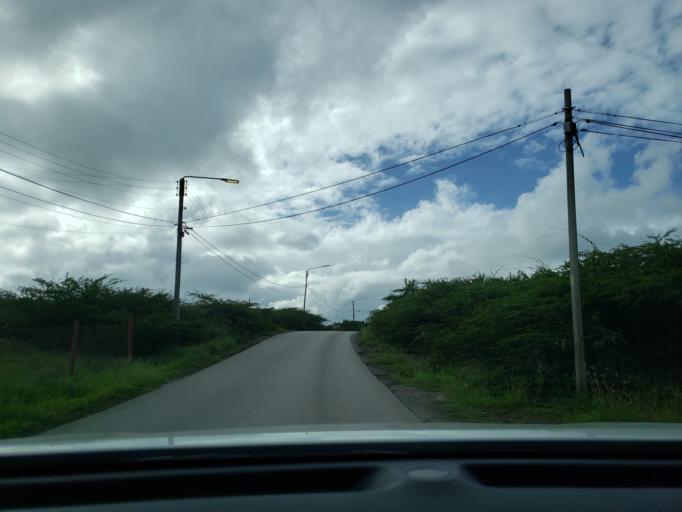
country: CW
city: Dorp Soto
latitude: 12.2156
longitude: -69.0607
